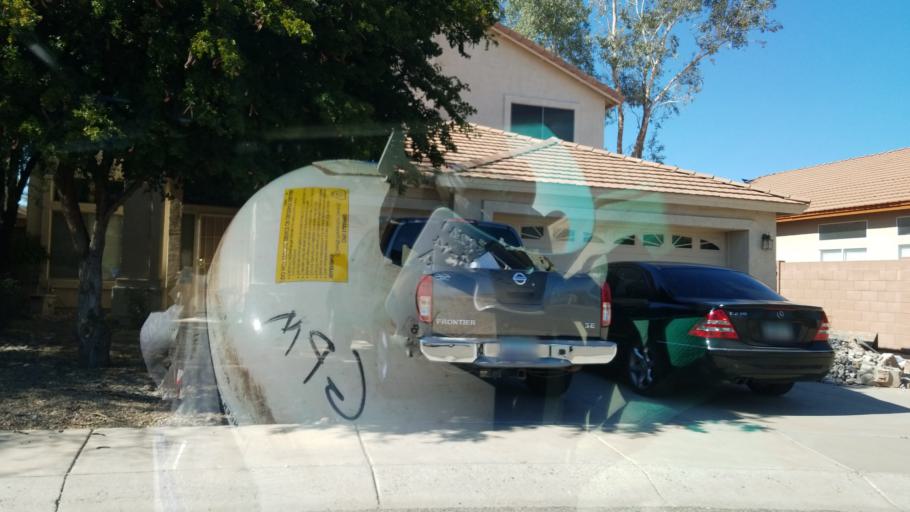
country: US
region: Arizona
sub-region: Maricopa County
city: Paradise Valley
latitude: 33.6472
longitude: -112.0457
